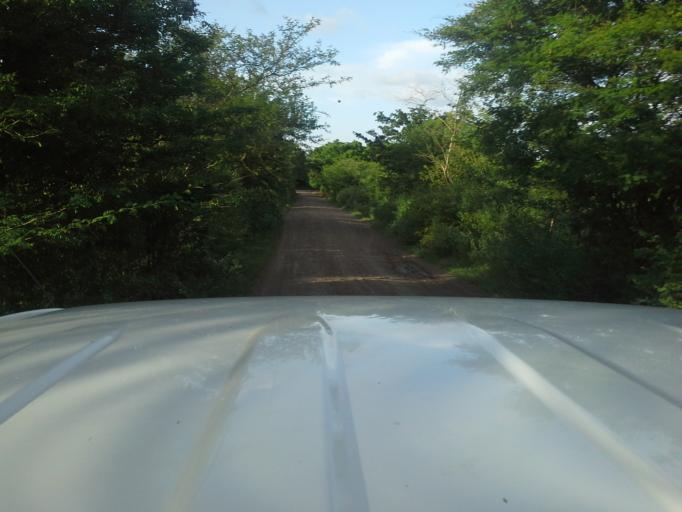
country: NI
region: Matagalpa
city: Ciudad Dario
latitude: 12.7909
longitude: -86.1559
